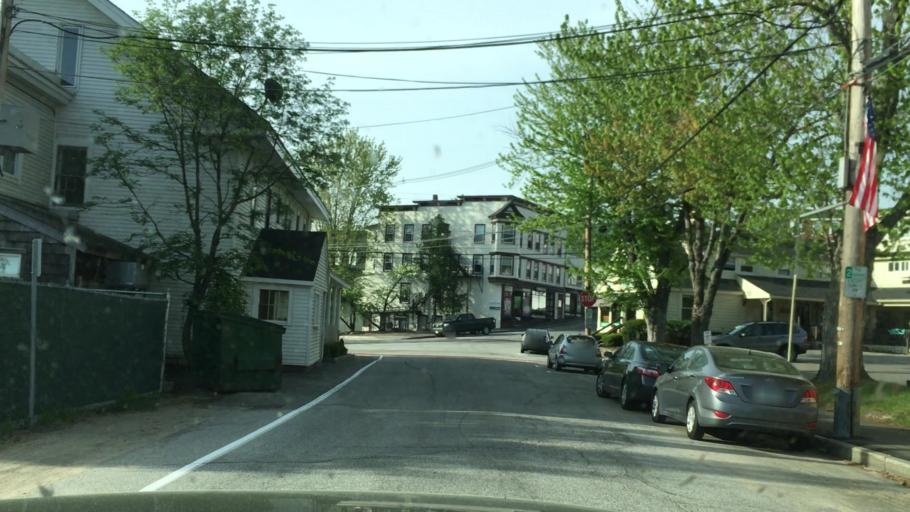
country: US
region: New Hampshire
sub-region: Belknap County
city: Meredith
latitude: 43.6583
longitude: -71.5009
